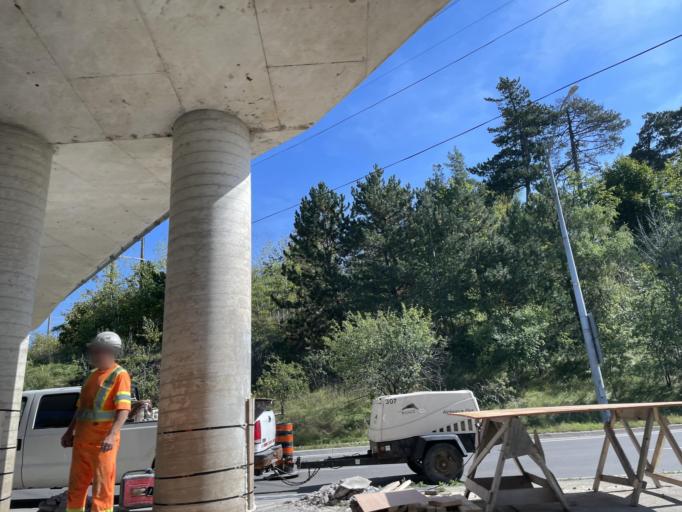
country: CA
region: Ontario
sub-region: Wellington County
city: Guelph
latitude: 43.5321
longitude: -80.2750
